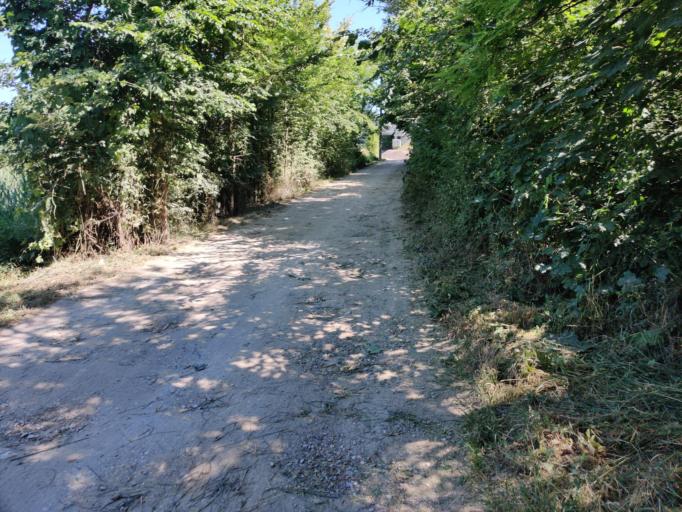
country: HU
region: Hajdu-Bihar
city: Balmazujvaros
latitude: 47.6032
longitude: 21.3791
